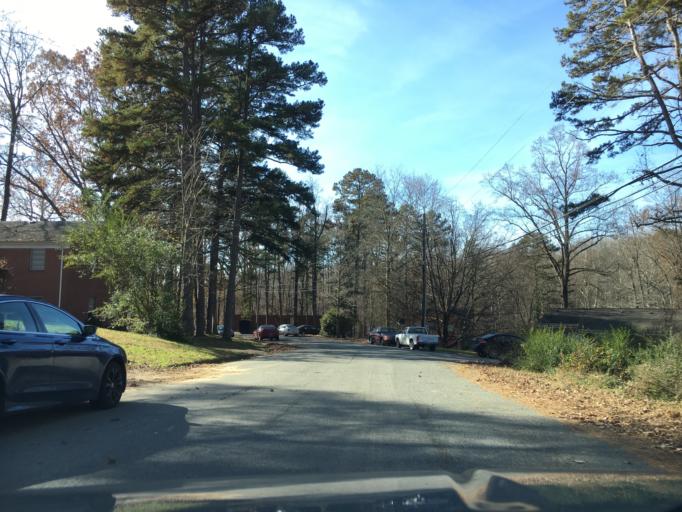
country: US
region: Virginia
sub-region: Halifax County
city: South Boston
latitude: 36.7089
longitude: -78.9118
